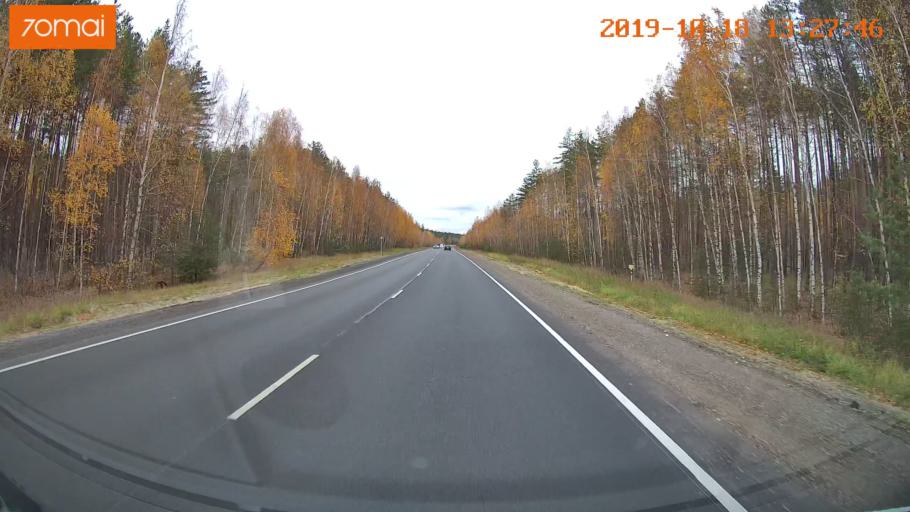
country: RU
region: Rjazan
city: Solotcha
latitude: 54.7688
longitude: 39.8589
